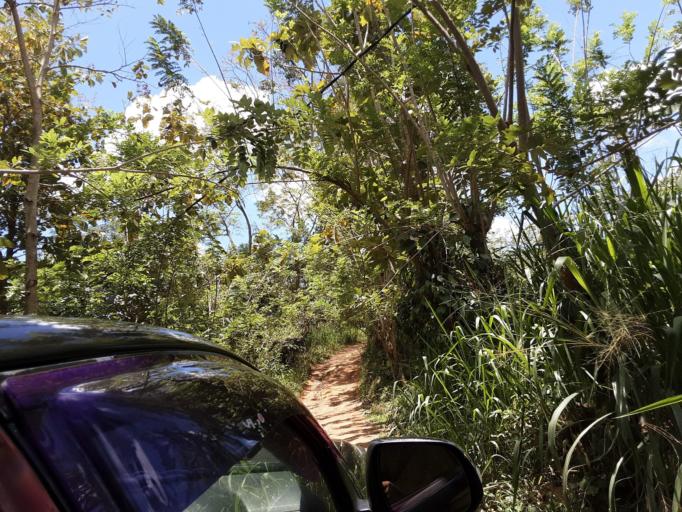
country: LK
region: Uva
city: Haputale
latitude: 6.8220
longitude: 81.1097
